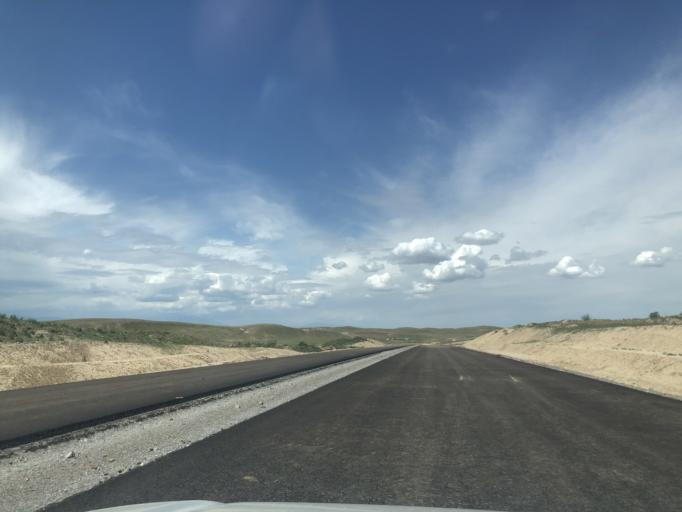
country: KG
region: Chuy
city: Bystrovka
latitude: 43.3007
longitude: 76.1214
